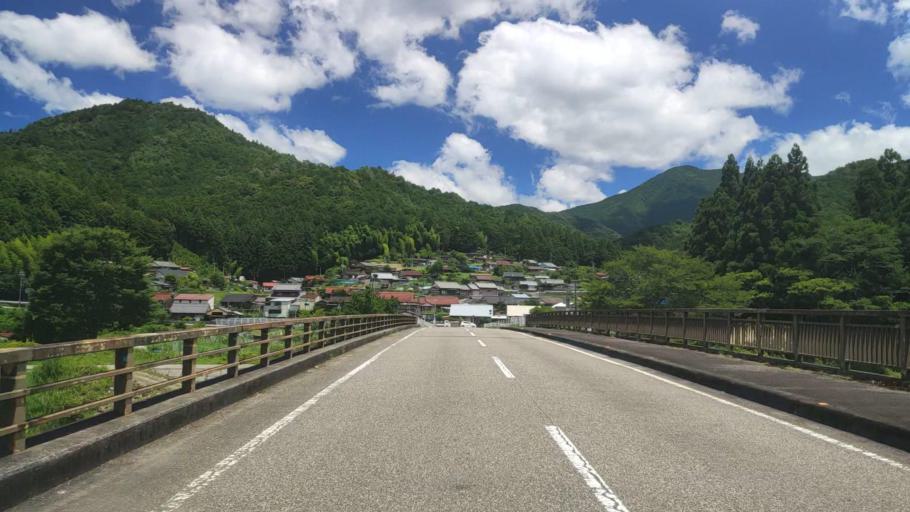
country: JP
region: Mie
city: Owase
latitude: 33.9829
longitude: 136.0396
